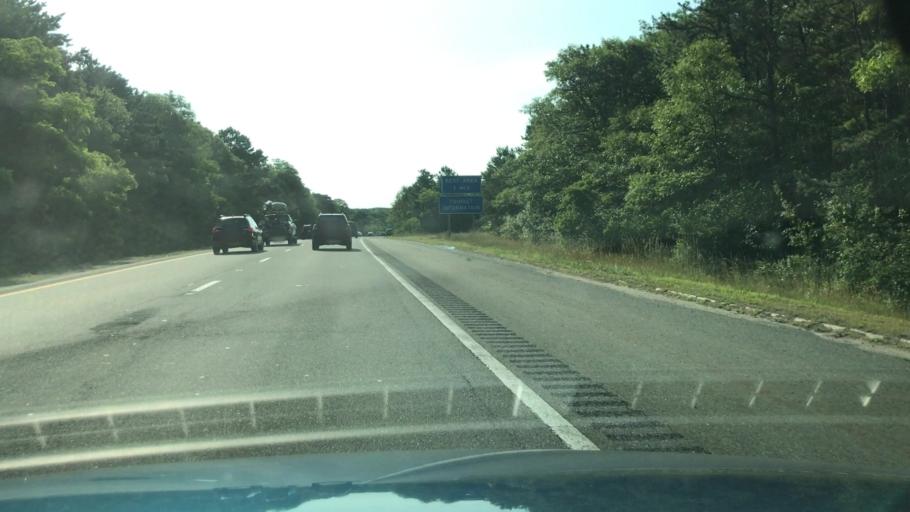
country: US
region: Massachusetts
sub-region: Barnstable County
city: Barnstable
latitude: 41.6895
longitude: -70.3149
